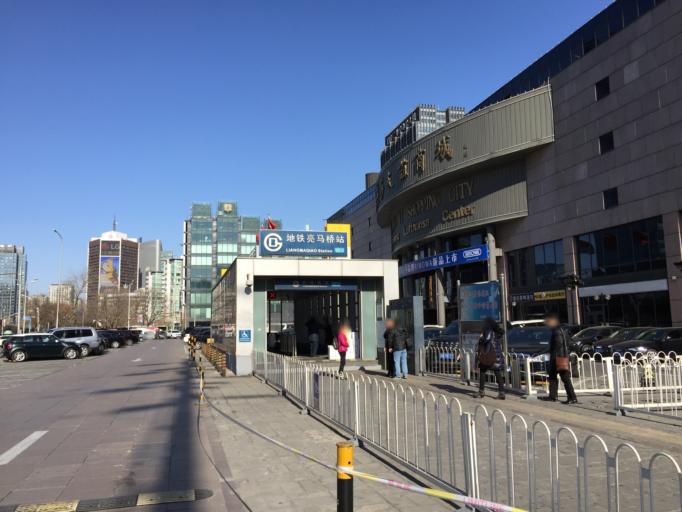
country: CN
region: Beijing
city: Chaowai
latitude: 39.9469
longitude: 116.4564
